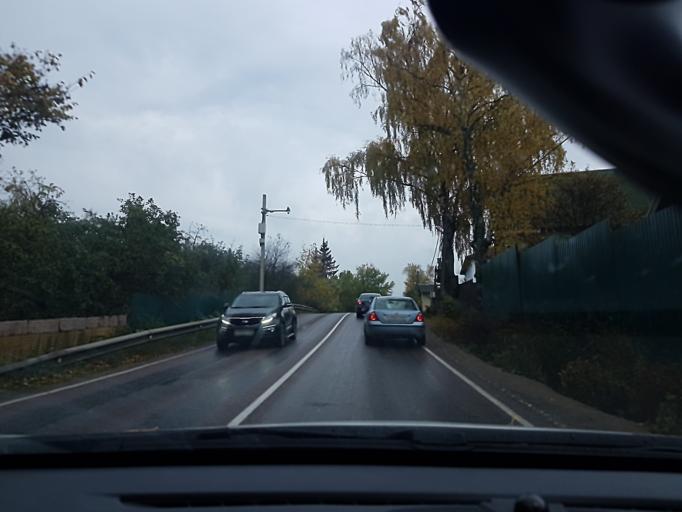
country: RU
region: Moskovskaya
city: Istra
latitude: 55.8899
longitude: 36.7965
